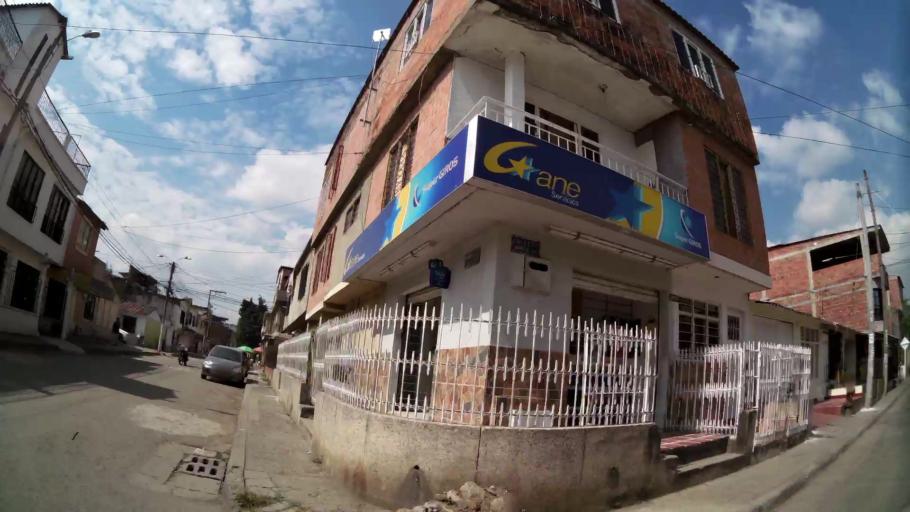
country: CO
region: Valle del Cauca
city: Cali
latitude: 3.4926
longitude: -76.4942
